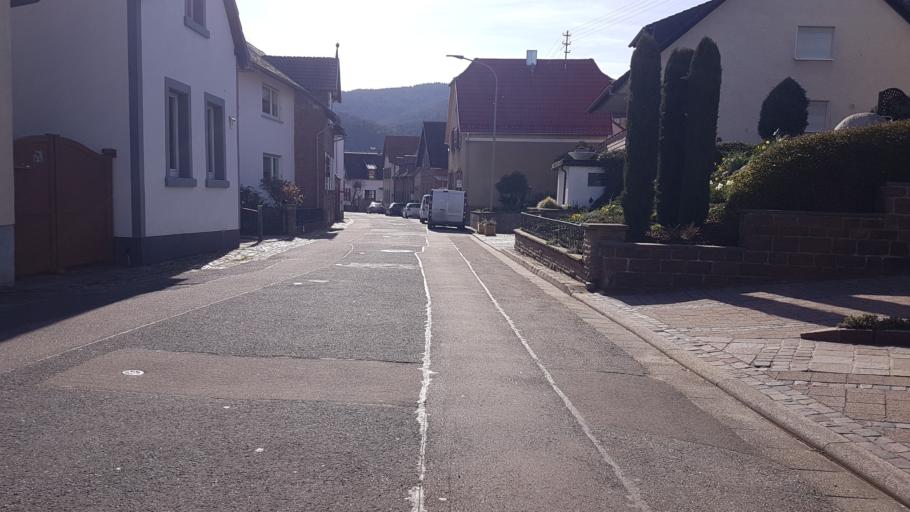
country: DE
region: Rheinland-Pfalz
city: Sankt Martin
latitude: 49.3029
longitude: 8.1059
